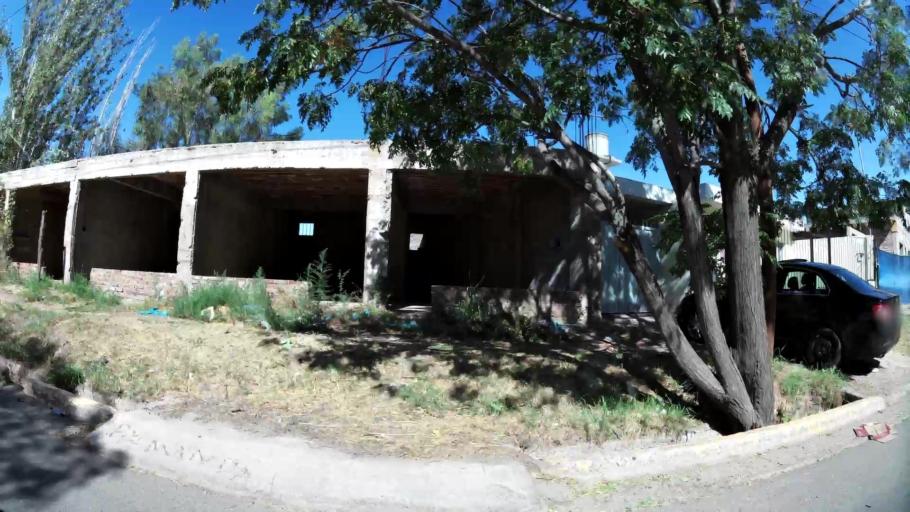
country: AR
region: Mendoza
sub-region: Departamento de Godoy Cruz
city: Godoy Cruz
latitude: -32.9497
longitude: -68.8207
